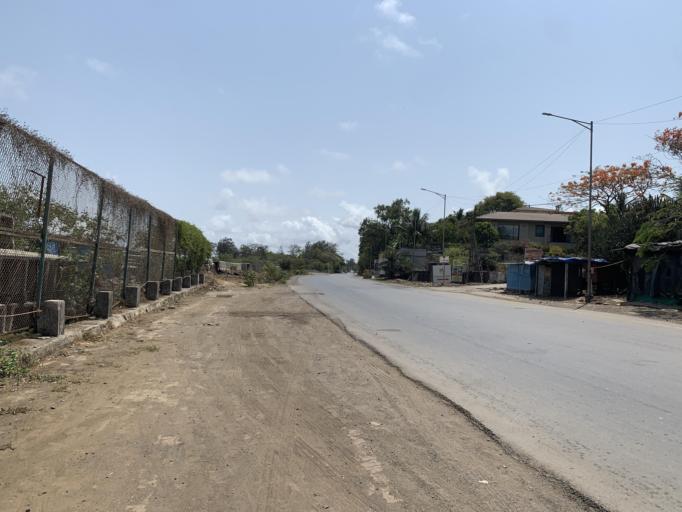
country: IN
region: Daman and Diu
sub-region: Daman District
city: Daman
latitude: 20.4551
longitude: 72.8404
